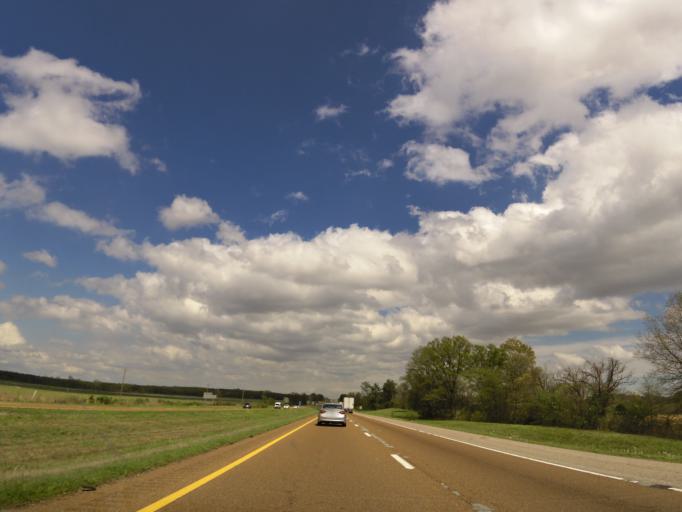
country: US
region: Tennessee
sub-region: Tipton County
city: Mason
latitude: 35.3548
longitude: -89.5053
